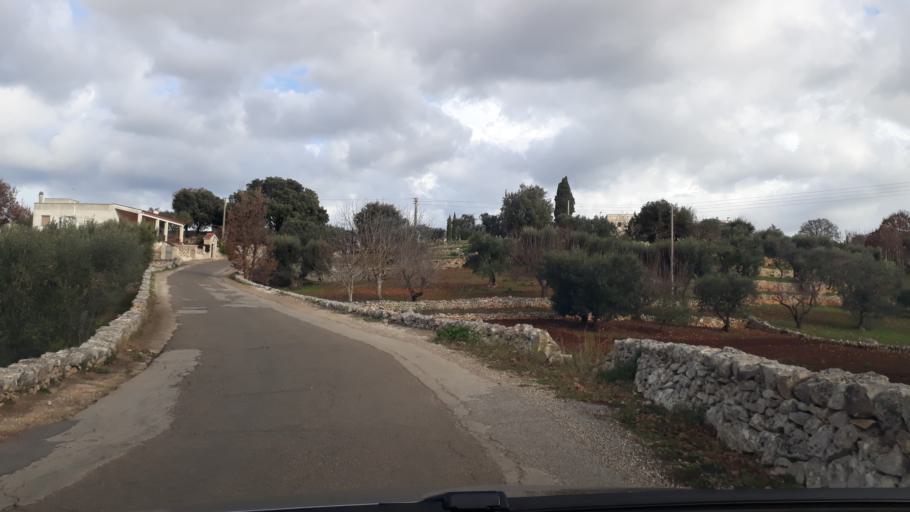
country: IT
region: Apulia
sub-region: Provincia di Brindisi
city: Cisternino
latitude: 40.7225
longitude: 17.4271
